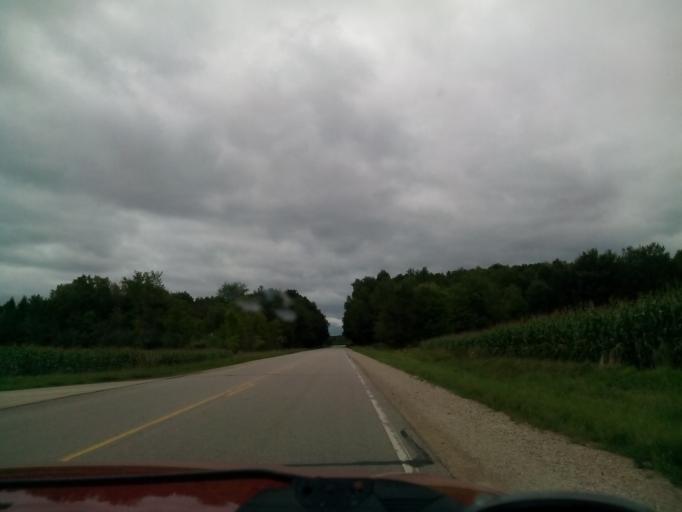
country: US
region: Wisconsin
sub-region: Menominee County
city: Legend Lake
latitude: 44.9965
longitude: -88.4378
